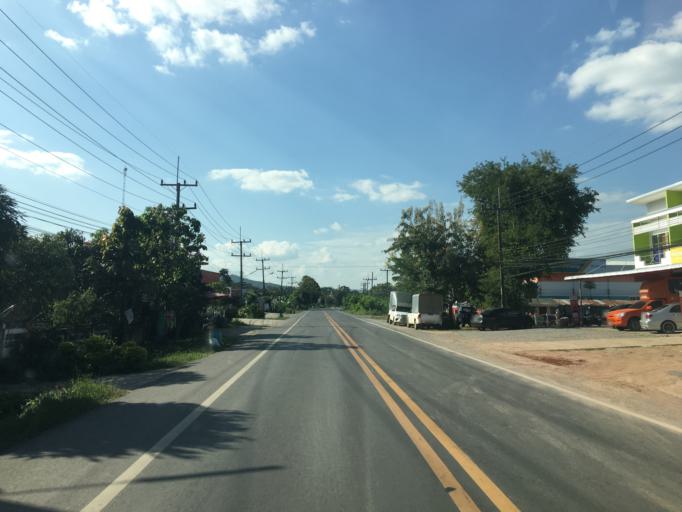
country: TH
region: Phayao
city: Chun
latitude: 19.3443
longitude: 100.1191
